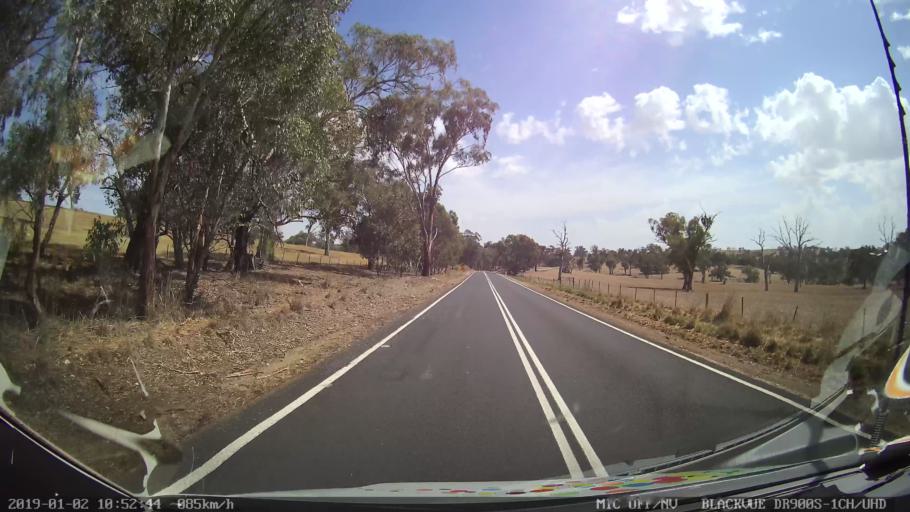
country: AU
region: New South Wales
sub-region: Cootamundra
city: Cootamundra
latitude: -34.6854
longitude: 148.2714
